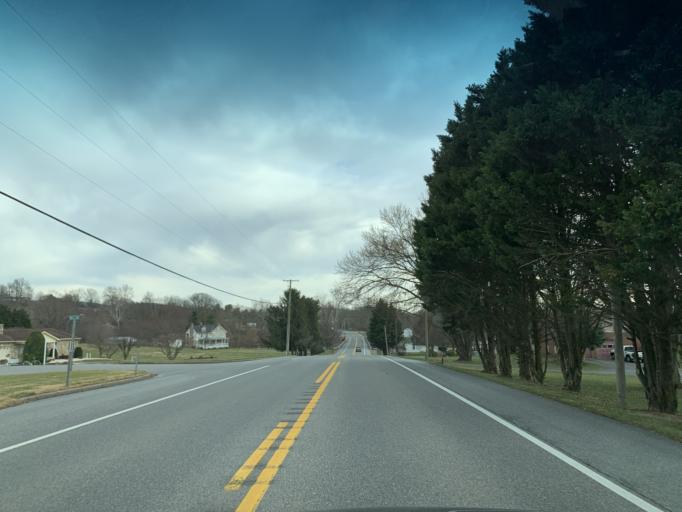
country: US
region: Maryland
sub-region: Washington County
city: Boonsboro
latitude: 39.5537
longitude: -77.6809
